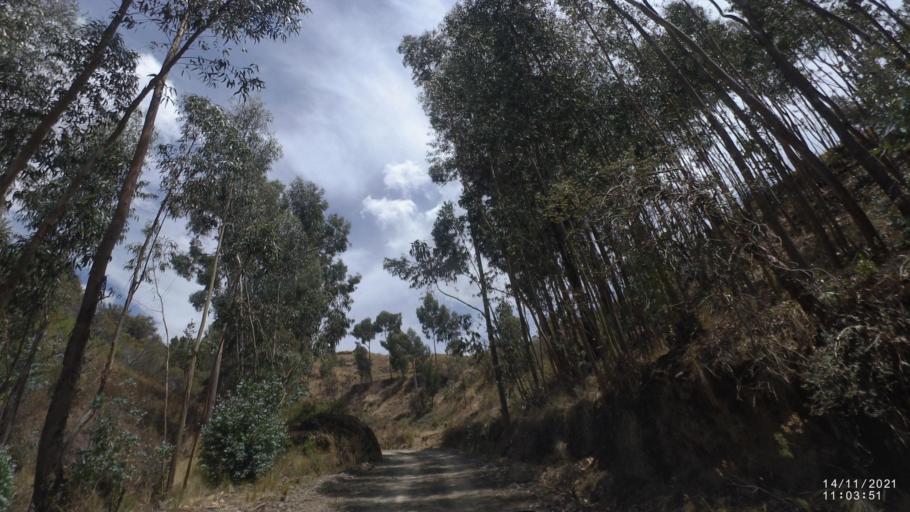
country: BO
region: Cochabamba
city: Cochabamba
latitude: -17.3359
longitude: -66.0597
